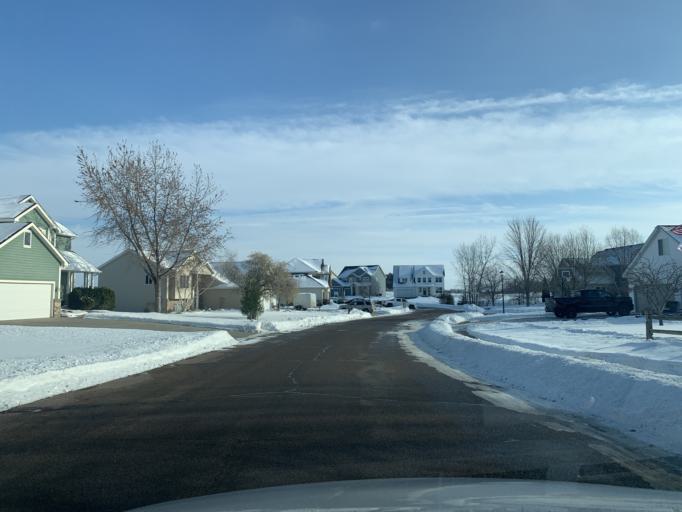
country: US
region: Minnesota
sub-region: Wright County
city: Buffalo
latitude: 45.2038
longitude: -93.8324
